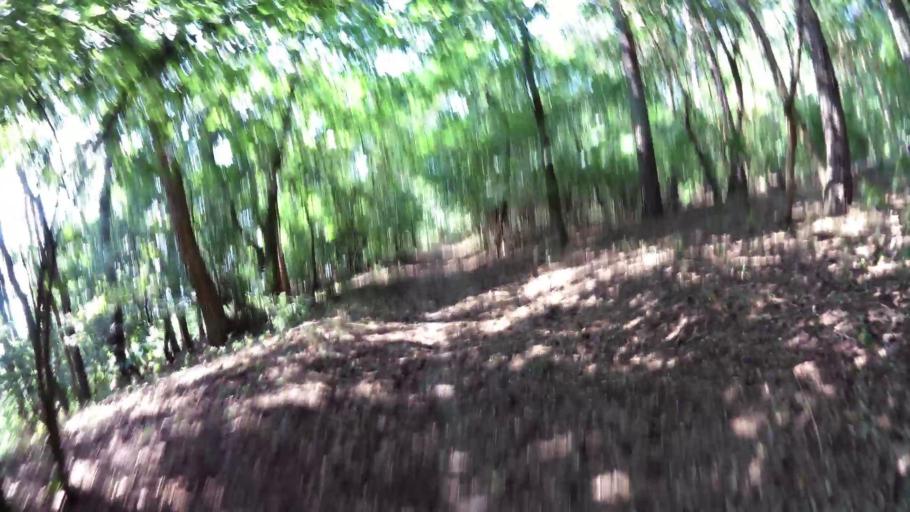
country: PL
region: West Pomeranian Voivodeship
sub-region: Powiat gryfinski
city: Moryn
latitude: 52.8674
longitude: 14.4194
